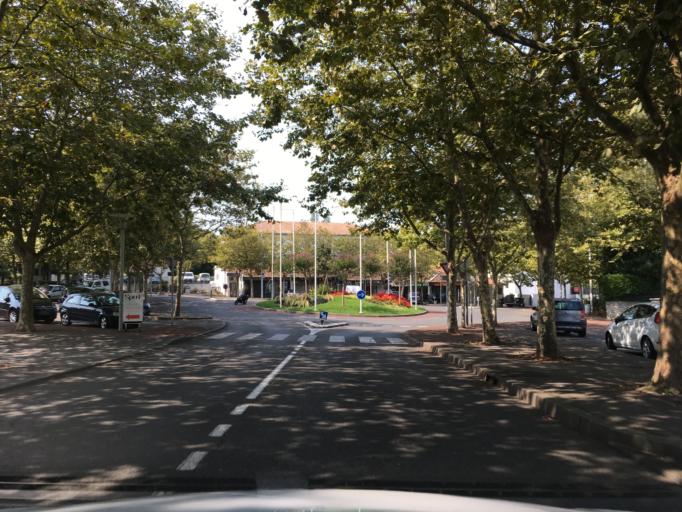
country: FR
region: Aquitaine
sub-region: Departement des Pyrenees-Atlantiques
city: Biarritz
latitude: 43.4964
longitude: -1.5376
